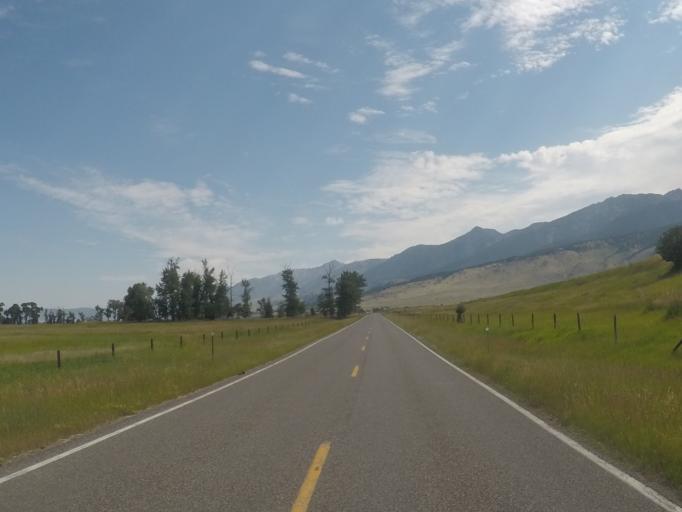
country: US
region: Montana
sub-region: Park County
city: Livingston
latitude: 45.4219
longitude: -110.6285
